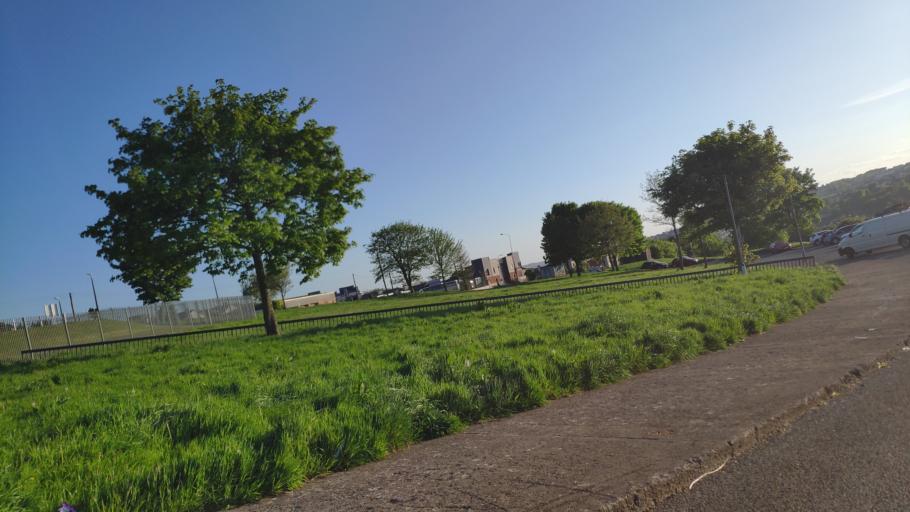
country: IE
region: Munster
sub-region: County Cork
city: Cork
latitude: 51.9118
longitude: -8.4642
